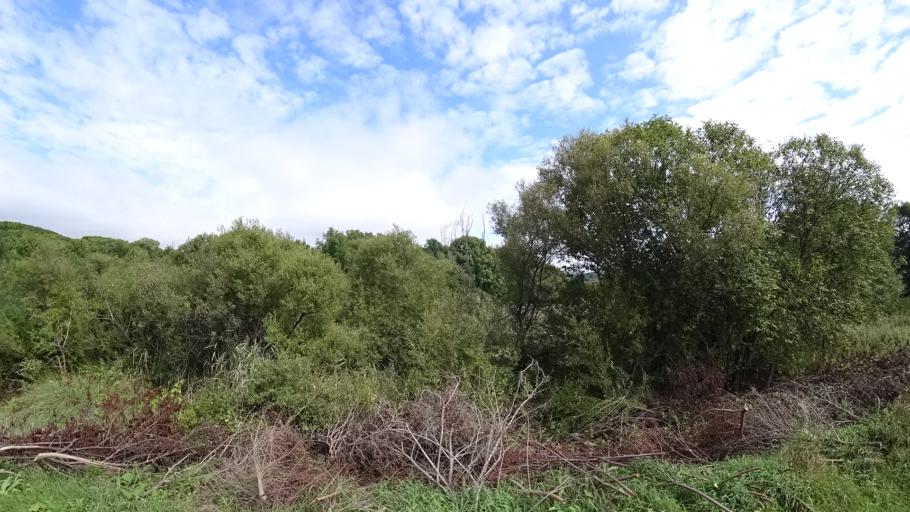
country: RU
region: Primorskiy
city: Lyalichi
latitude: 44.1358
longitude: 132.3875
